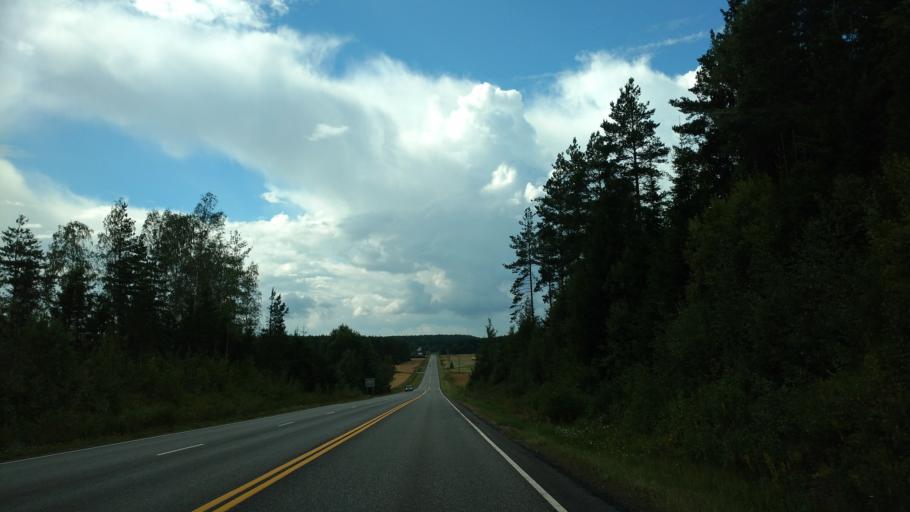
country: FI
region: Varsinais-Suomi
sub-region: Turku
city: Sauvo
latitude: 60.4051
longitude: 22.8164
